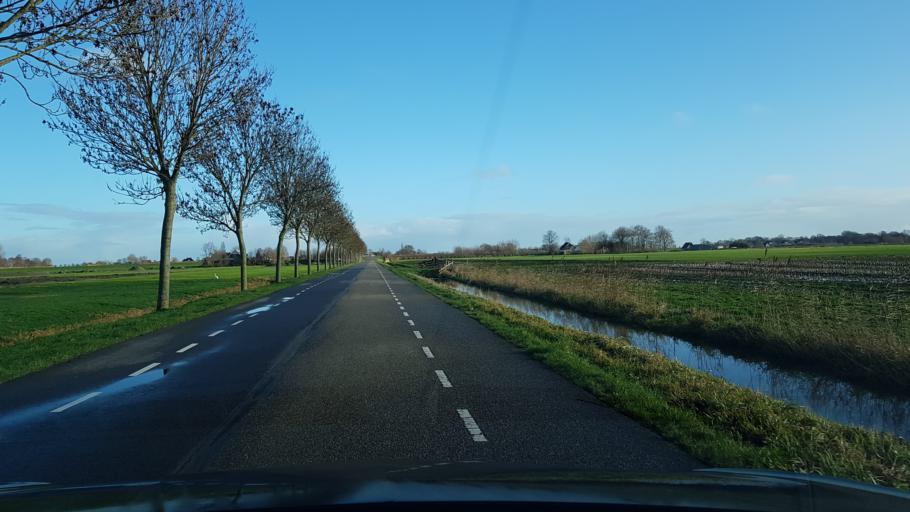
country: NL
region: South Holland
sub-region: Gemeente Nieuwkoop
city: Nieuwkoop
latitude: 52.1872
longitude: 4.8125
